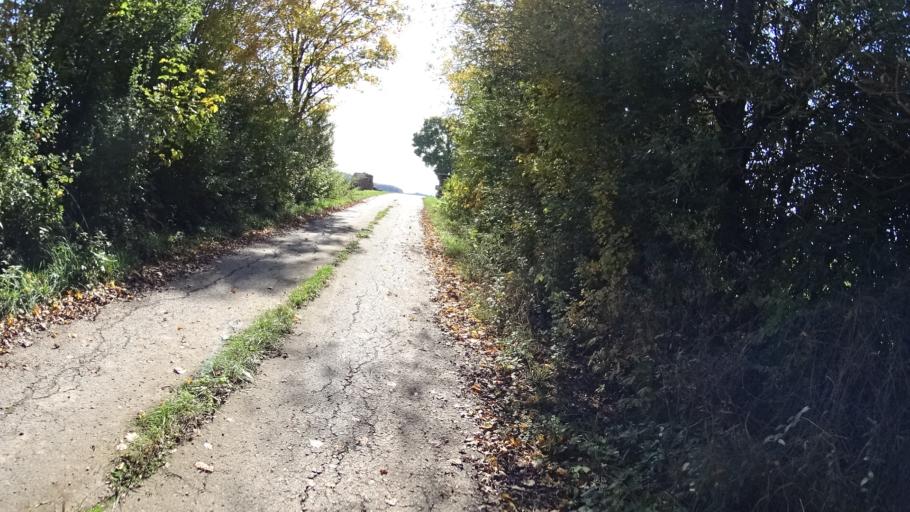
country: DE
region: Bavaria
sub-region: Upper Bavaria
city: Hitzhofen
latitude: 48.8619
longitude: 11.3341
